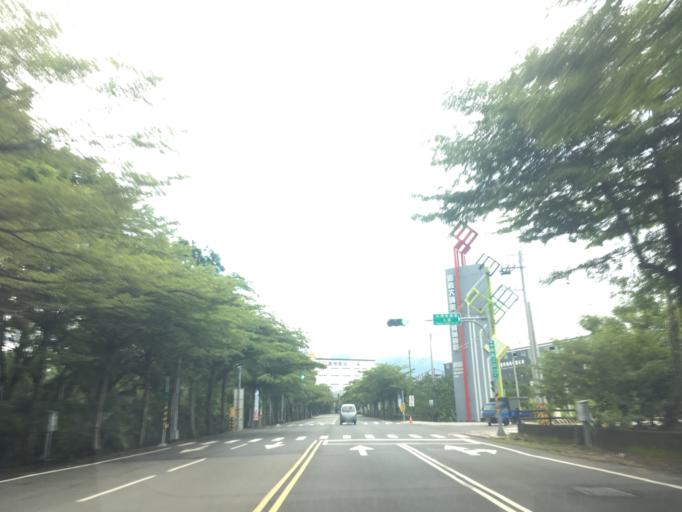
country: TW
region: Taiwan
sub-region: Yunlin
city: Douliu
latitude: 23.5938
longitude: 120.5269
